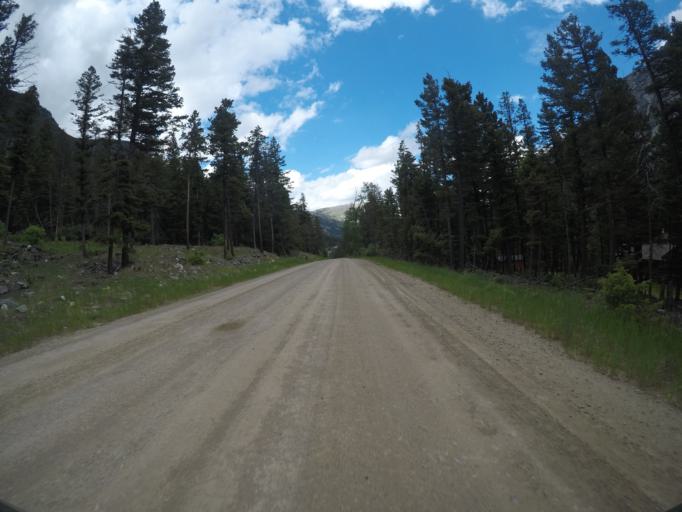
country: US
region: Montana
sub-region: Park County
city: Livingston
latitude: 45.4968
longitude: -110.2262
